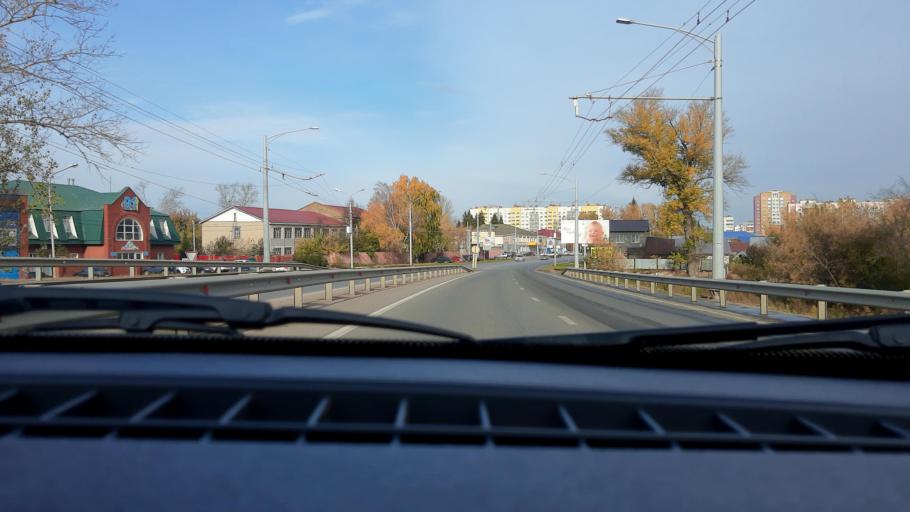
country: RU
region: Bashkortostan
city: Mikhaylovka
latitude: 54.7759
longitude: 55.8928
